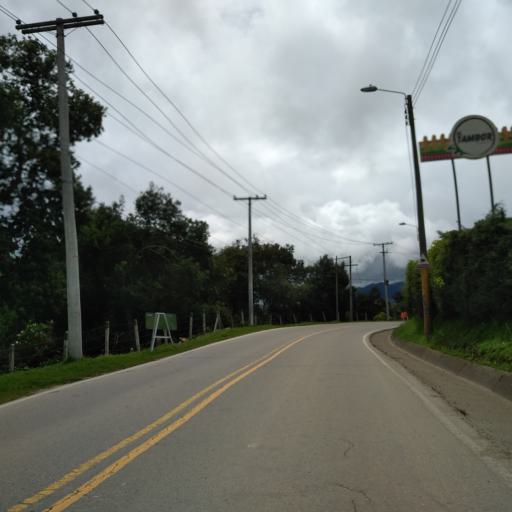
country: CO
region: Cundinamarca
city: La Calera
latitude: 4.6961
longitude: -73.9857
